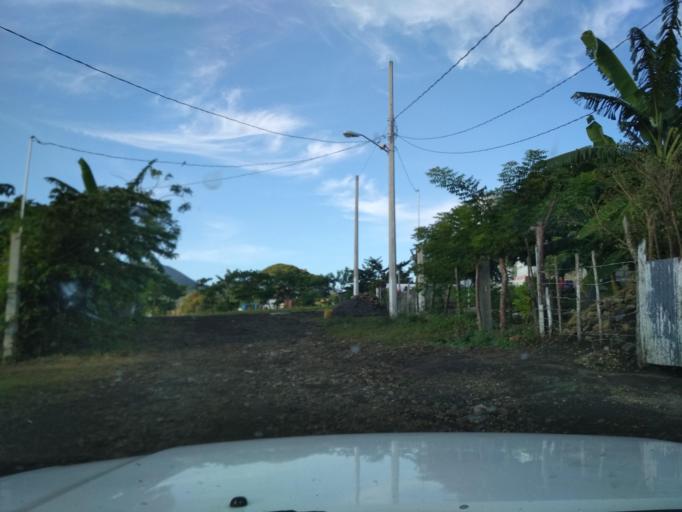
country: MX
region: Veracruz
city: Catemaco
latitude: 18.4210
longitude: -95.1225
